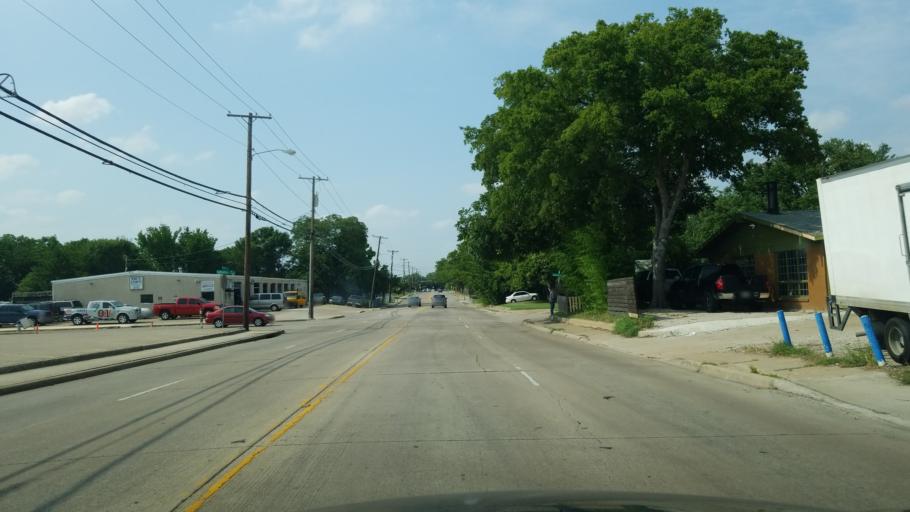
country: US
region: Texas
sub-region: Dallas County
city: Farmers Branch
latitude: 32.9000
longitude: -96.8814
